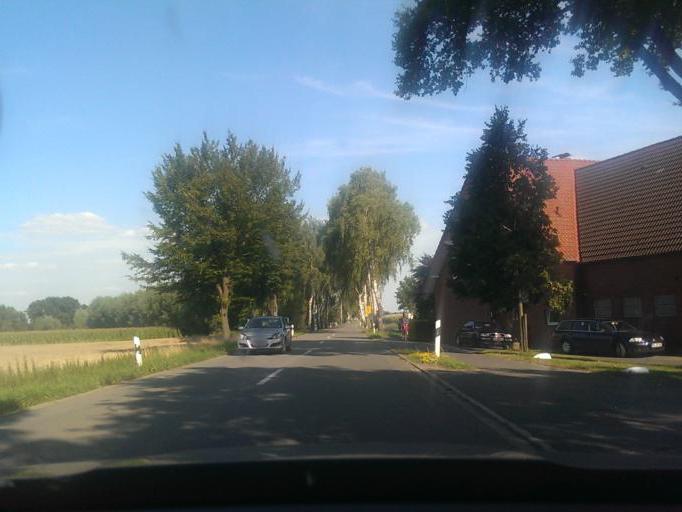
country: DE
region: North Rhine-Westphalia
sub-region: Regierungsbezirk Detmold
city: Delbruck
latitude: 51.7380
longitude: 8.6001
